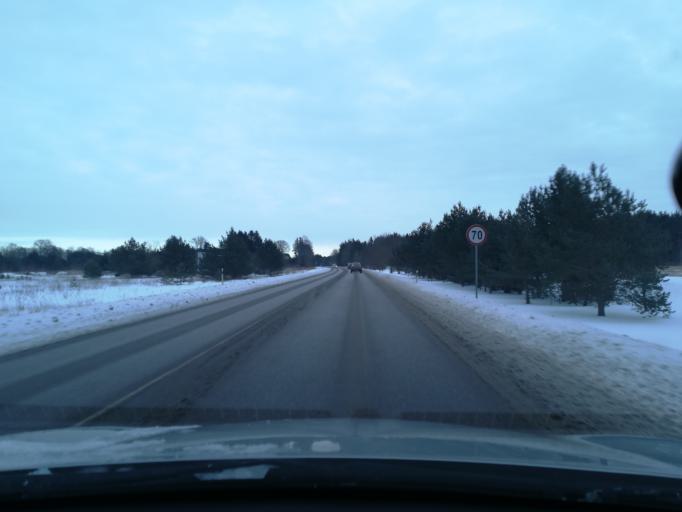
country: EE
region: Harju
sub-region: Harku vald
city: Tabasalu
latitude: 59.4335
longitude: 24.5909
